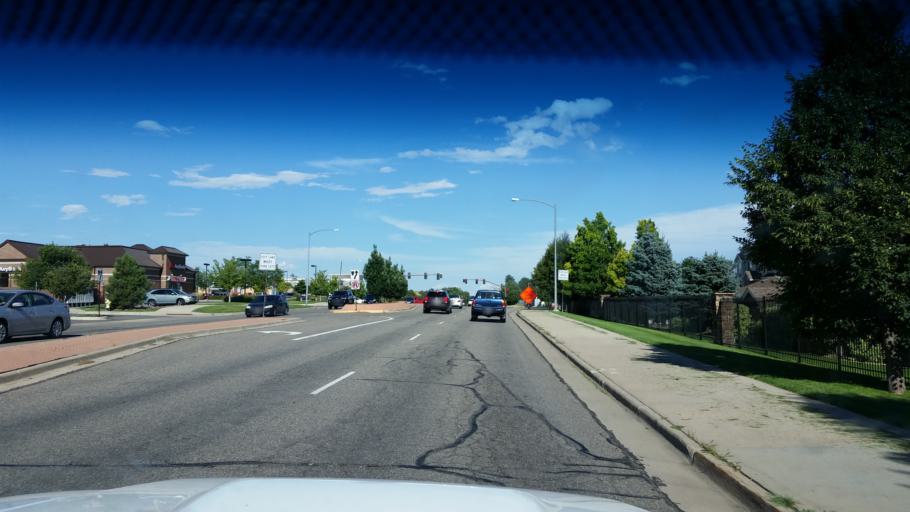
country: US
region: Colorado
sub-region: Adams County
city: Northglenn
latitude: 39.9283
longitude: -104.9423
